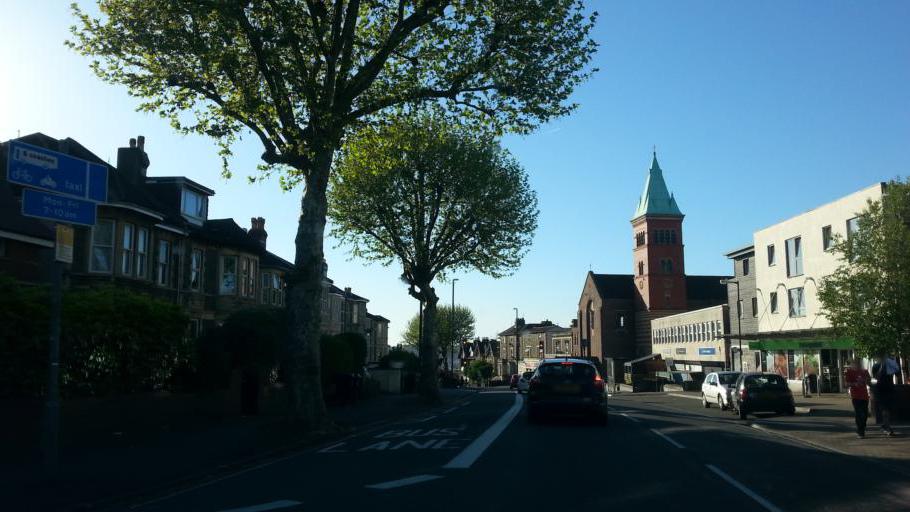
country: GB
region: England
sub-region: Bristol
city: Bristol
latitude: 51.4396
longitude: -2.5733
